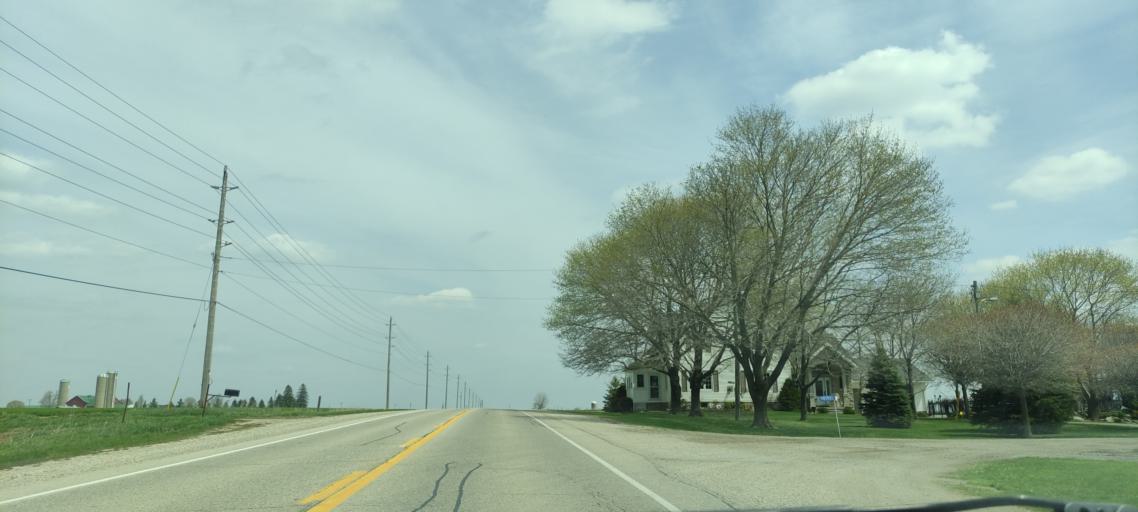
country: CA
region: Ontario
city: Stratford
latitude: 43.3475
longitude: -80.7535
